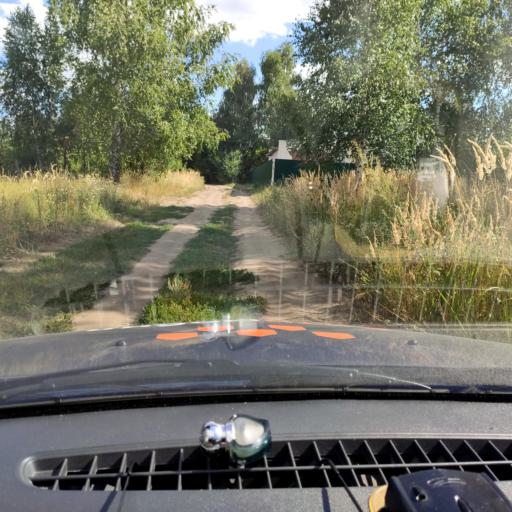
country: RU
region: Voronezj
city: Somovo
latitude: 51.7211
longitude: 39.3982
